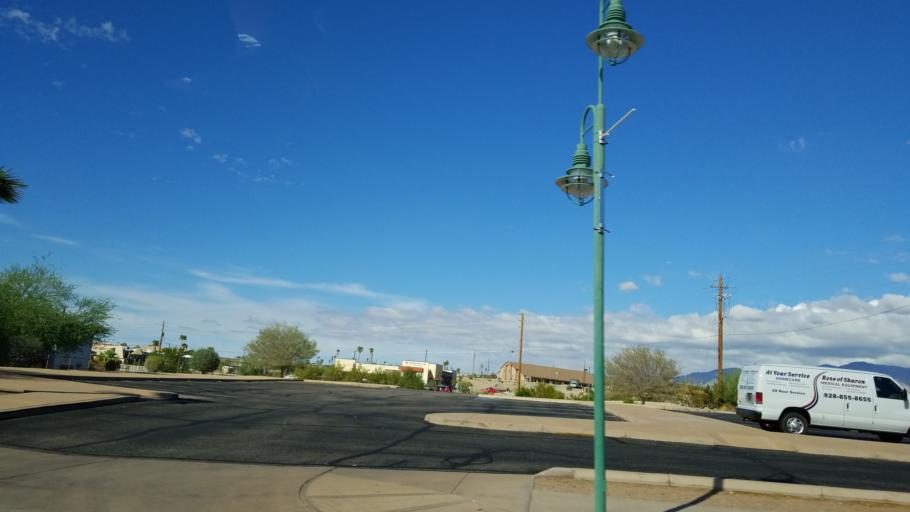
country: US
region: Arizona
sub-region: Mohave County
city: Lake Havasu City
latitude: 34.4750
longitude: -114.3268
